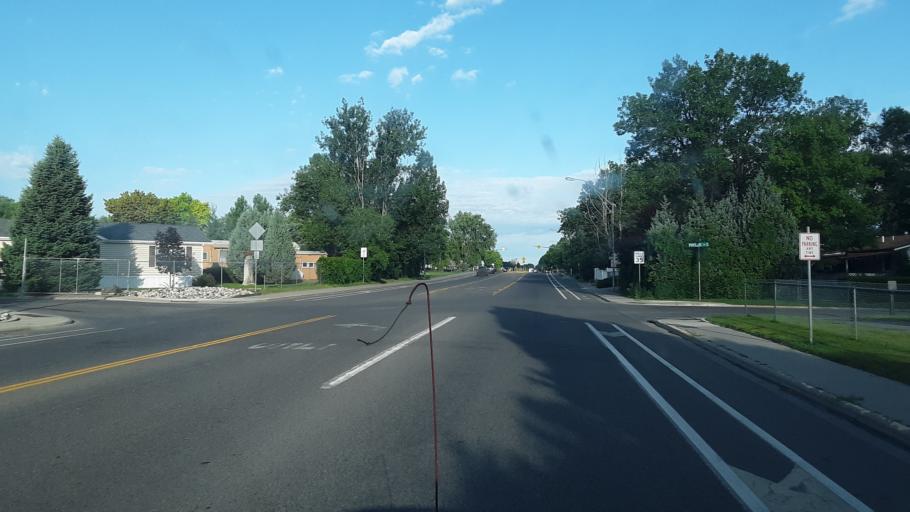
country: US
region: Montana
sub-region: Yellowstone County
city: Billings
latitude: 45.7625
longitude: -108.5837
